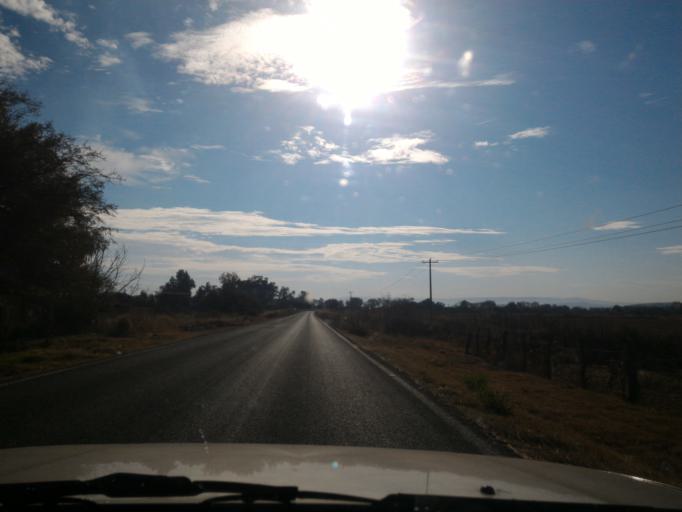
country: MX
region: Guanajuato
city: Ciudad Manuel Doblado
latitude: 20.7995
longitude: -101.9882
